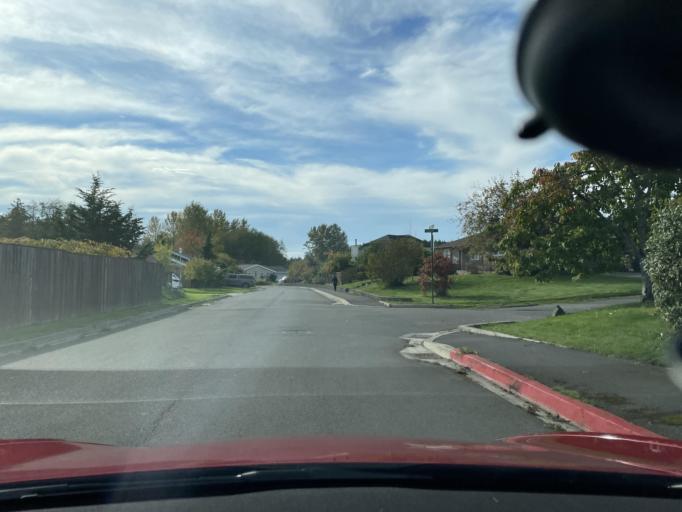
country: US
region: Washington
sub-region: San Juan County
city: Friday Harbor
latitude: 48.5278
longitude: -123.0208
